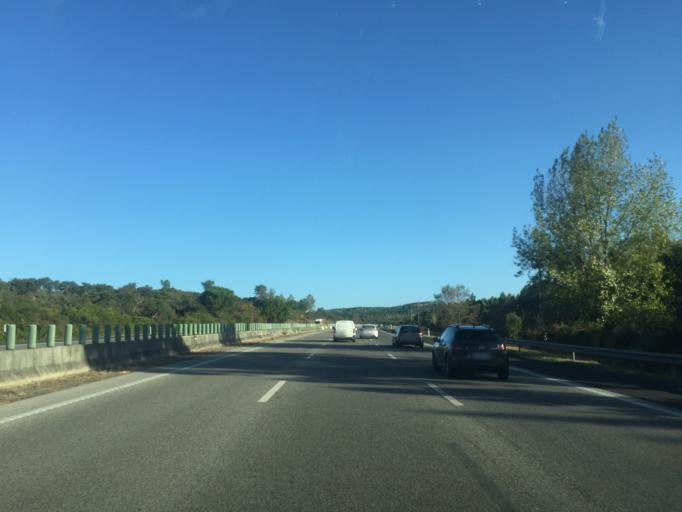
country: PT
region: Lisbon
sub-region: Azambuja
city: Azambuja
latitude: 39.0800
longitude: -8.9323
